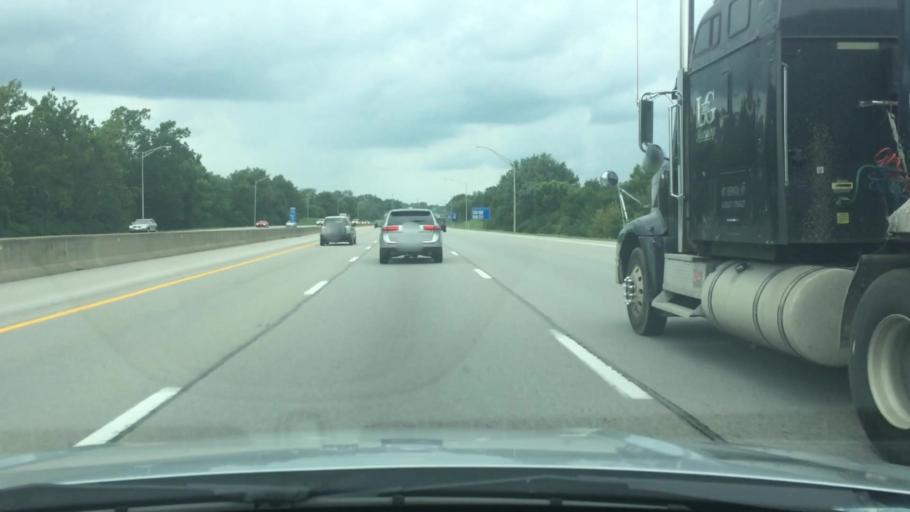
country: US
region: Kentucky
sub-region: Fayette County
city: Lexington-Fayette
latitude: 38.0620
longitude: -84.4382
